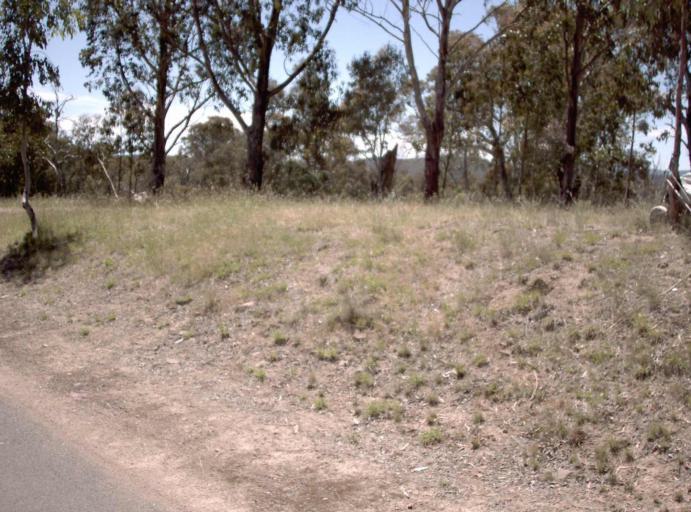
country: AU
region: New South Wales
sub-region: Snowy River
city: Jindabyne
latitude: -37.1119
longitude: 148.2500
